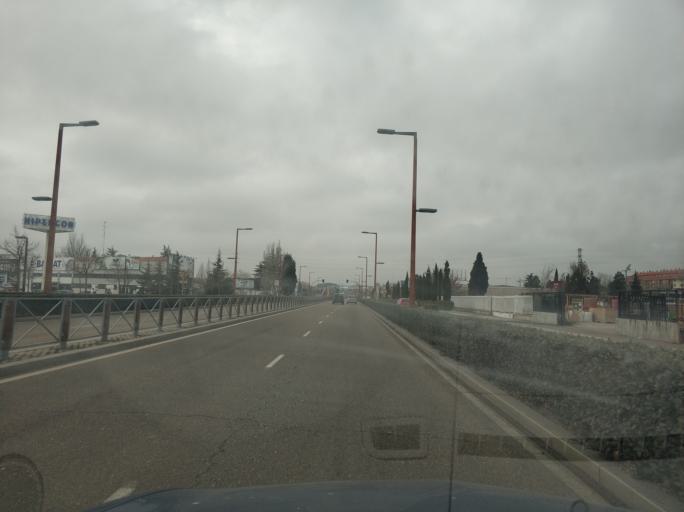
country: ES
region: Castille and Leon
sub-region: Provincia de Valladolid
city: Arroyo
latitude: 41.6238
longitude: -4.7701
